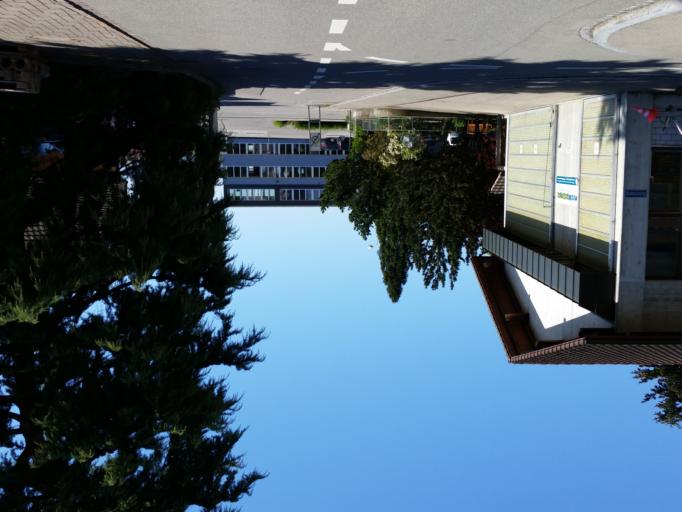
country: CH
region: Thurgau
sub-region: Arbon District
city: Salmsach
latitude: 47.5600
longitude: 9.3723
